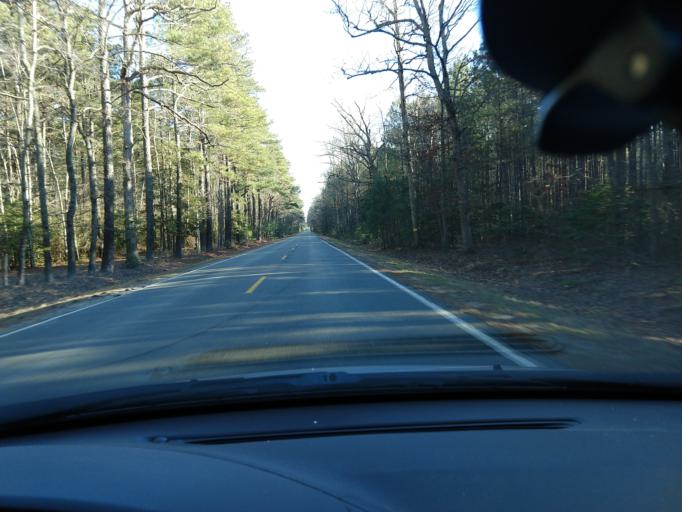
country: US
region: Virginia
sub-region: Surry County
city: Surry
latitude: 37.2727
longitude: -76.9049
